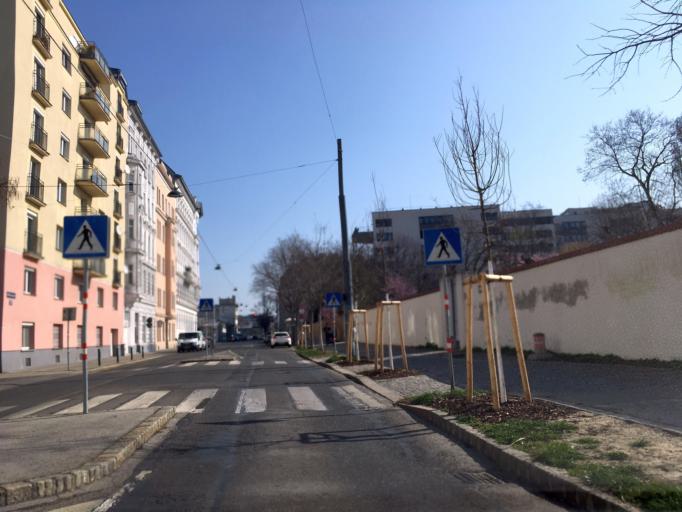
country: AT
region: Vienna
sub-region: Wien Stadt
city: Vienna
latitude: 48.2292
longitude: 16.3759
